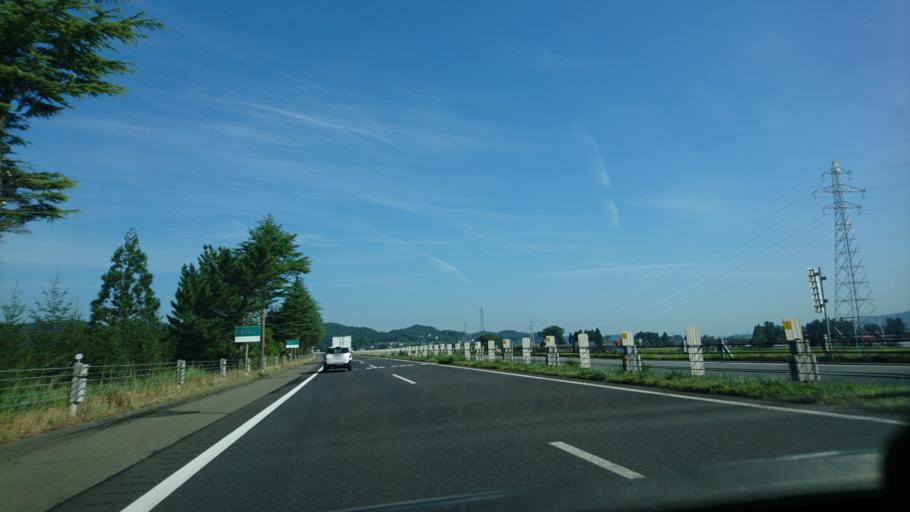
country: JP
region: Iwate
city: Ichinoseki
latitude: 38.9745
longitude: 141.1116
